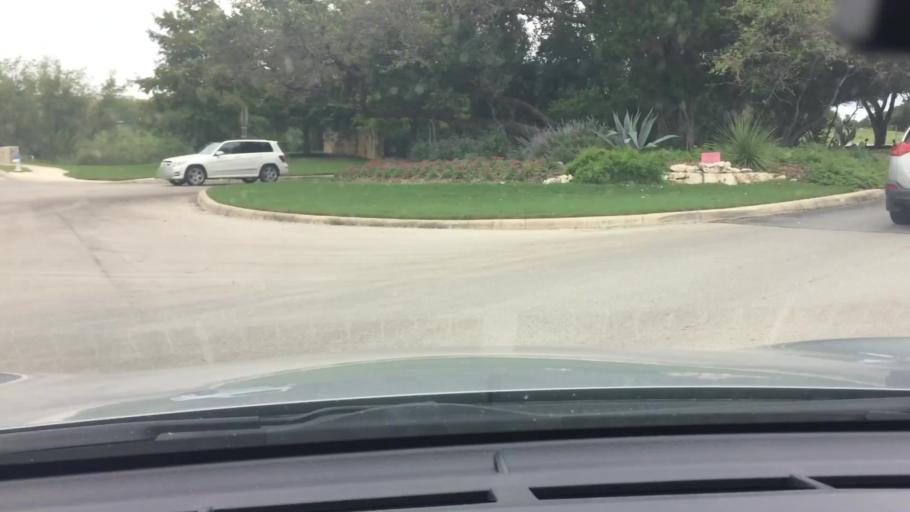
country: US
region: Texas
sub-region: Bexar County
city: Timberwood Park
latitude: 29.6623
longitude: -98.4011
